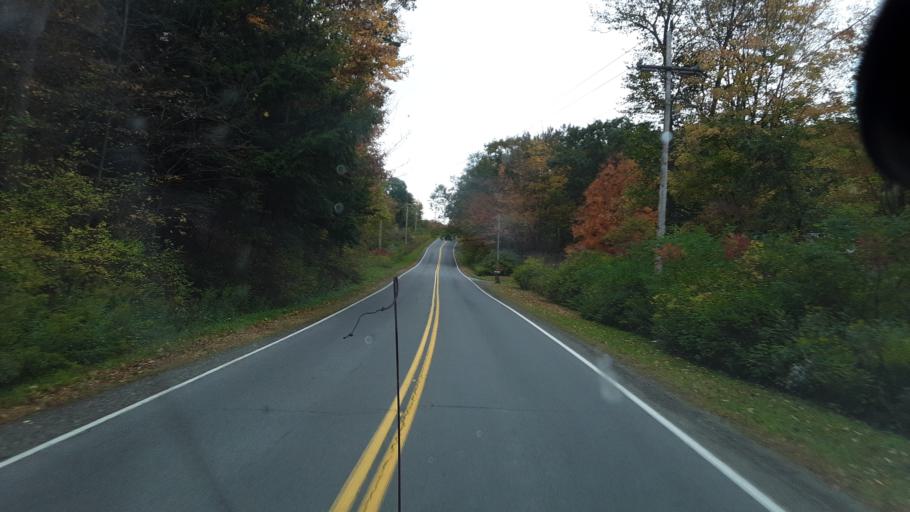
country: US
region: New York
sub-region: Steuben County
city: Canisteo
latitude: 42.2784
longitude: -77.6462
